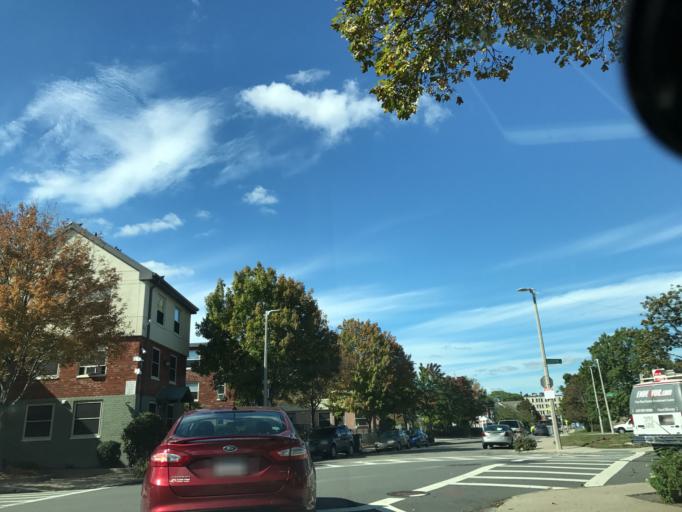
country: US
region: Massachusetts
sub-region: Suffolk County
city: South Boston
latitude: 42.3291
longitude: -71.0787
